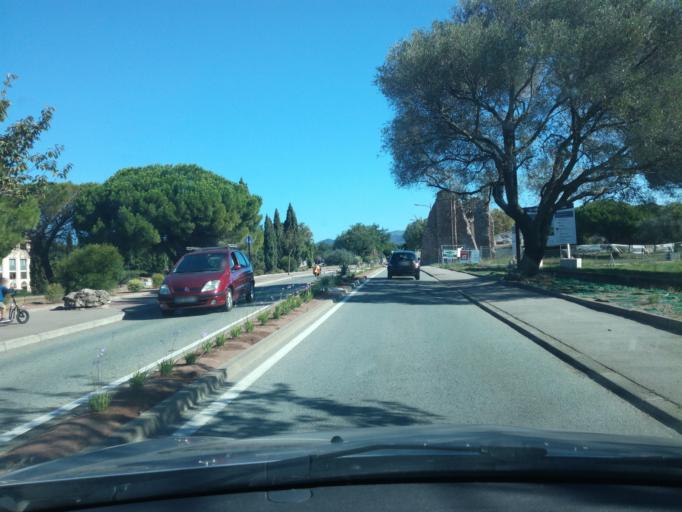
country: FR
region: Provence-Alpes-Cote d'Azur
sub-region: Departement du Var
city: Frejus
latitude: 43.4377
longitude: 6.7416
